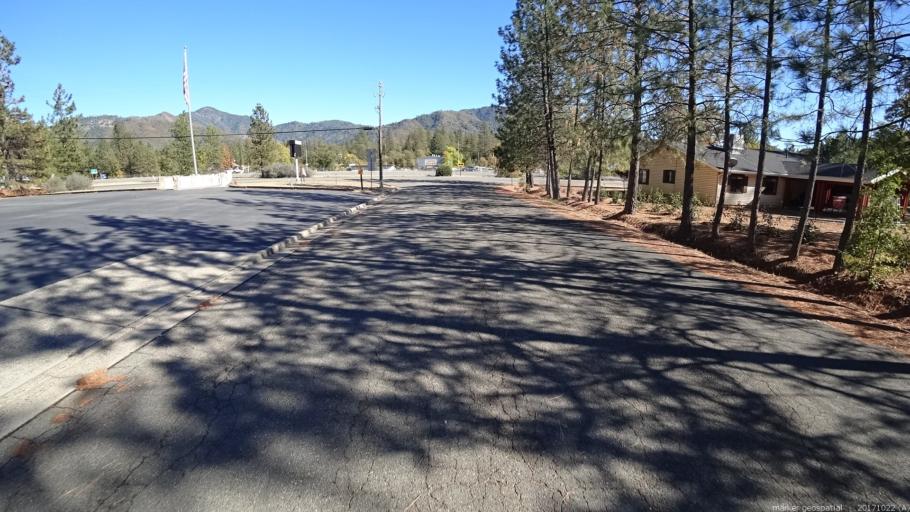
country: US
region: California
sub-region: Shasta County
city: Central Valley (historical)
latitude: 40.8897
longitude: -122.3847
